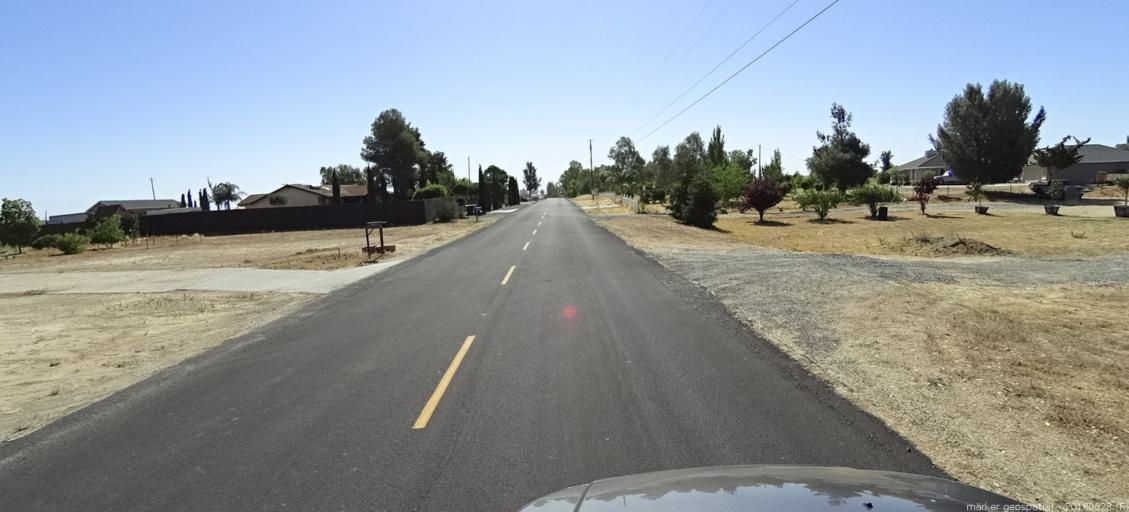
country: US
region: California
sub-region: Madera County
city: Bonadelle Ranchos-Madera Ranchos
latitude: 37.0085
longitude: -119.8794
